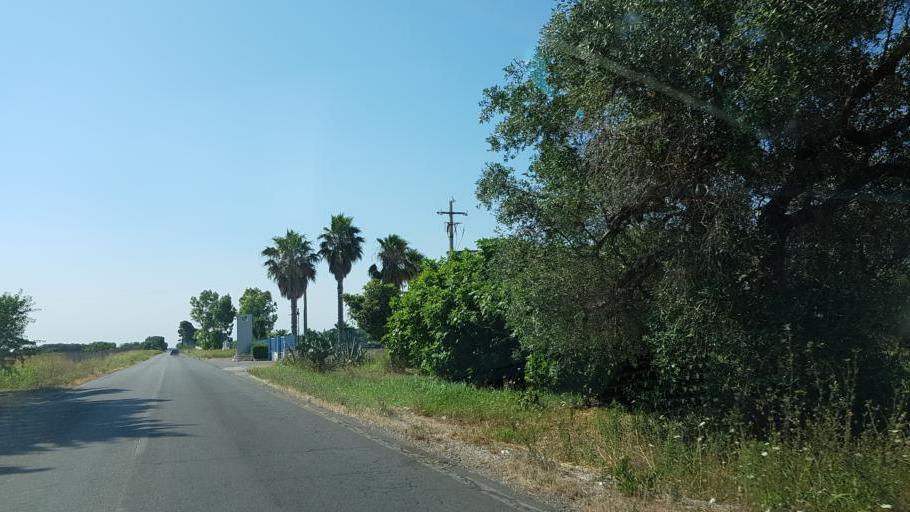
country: IT
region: Apulia
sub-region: Provincia di Brindisi
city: San Donaci
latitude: 40.4359
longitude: 17.9350
